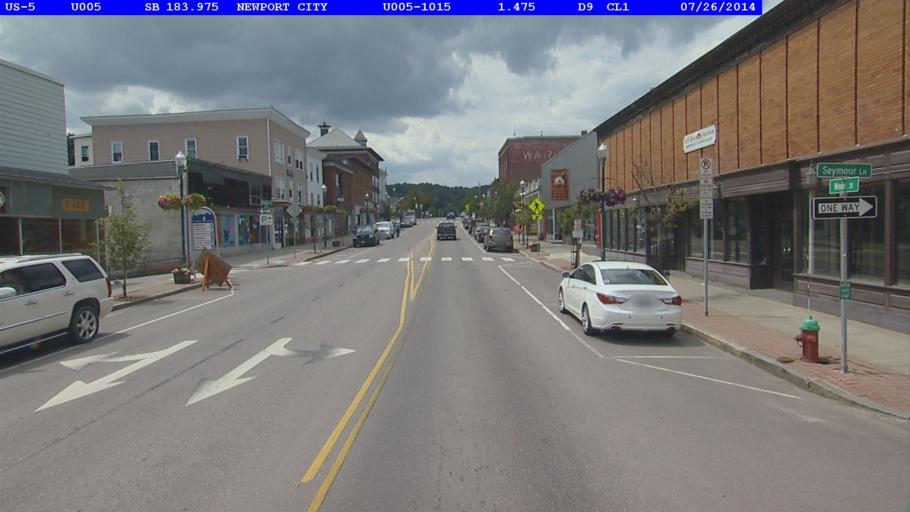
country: US
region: Vermont
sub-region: Orleans County
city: Newport
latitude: 44.9360
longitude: -72.2088
